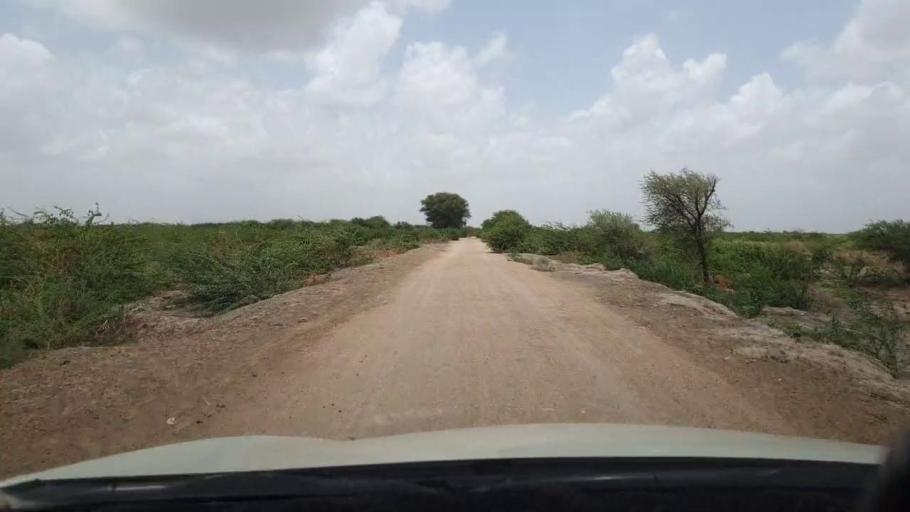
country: PK
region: Sindh
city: Kadhan
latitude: 24.3603
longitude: 68.9480
